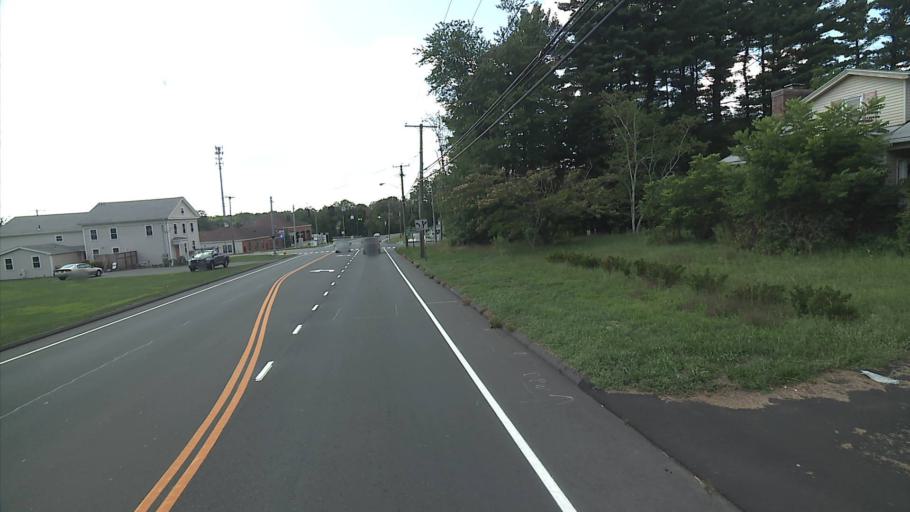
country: US
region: Connecticut
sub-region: Tolland County
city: Somers
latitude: 41.9844
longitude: -72.4623
